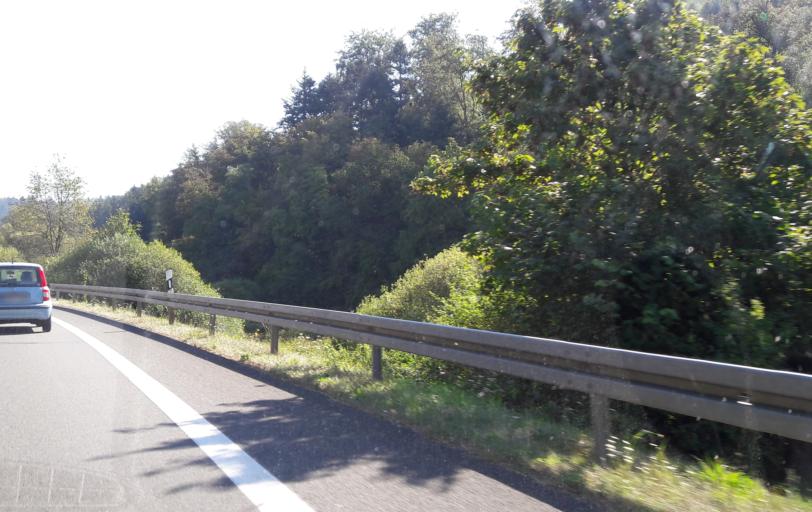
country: DE
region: Saarland
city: Nohfelden
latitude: 49.5704
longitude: 7.1026
